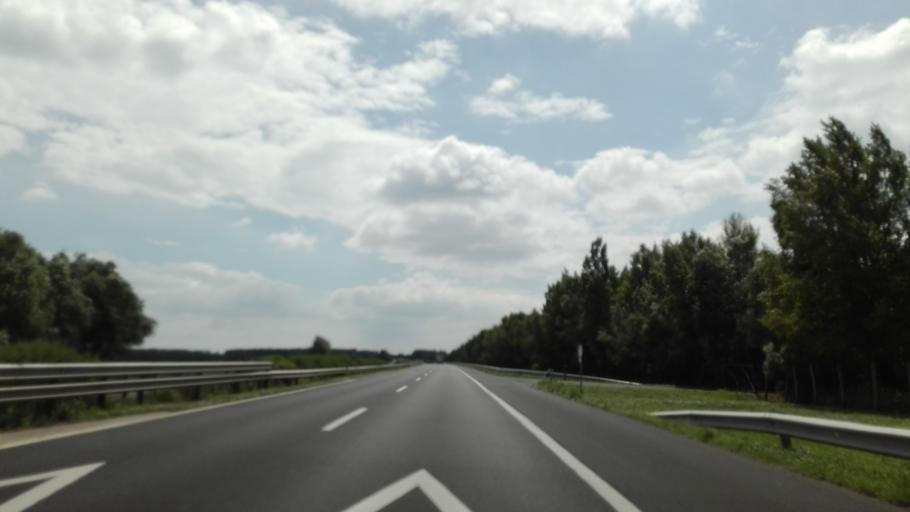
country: HU
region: Gyor-Moson-Sopron
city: Mosonmagyarovar
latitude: 47.8071
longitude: 17.2995
